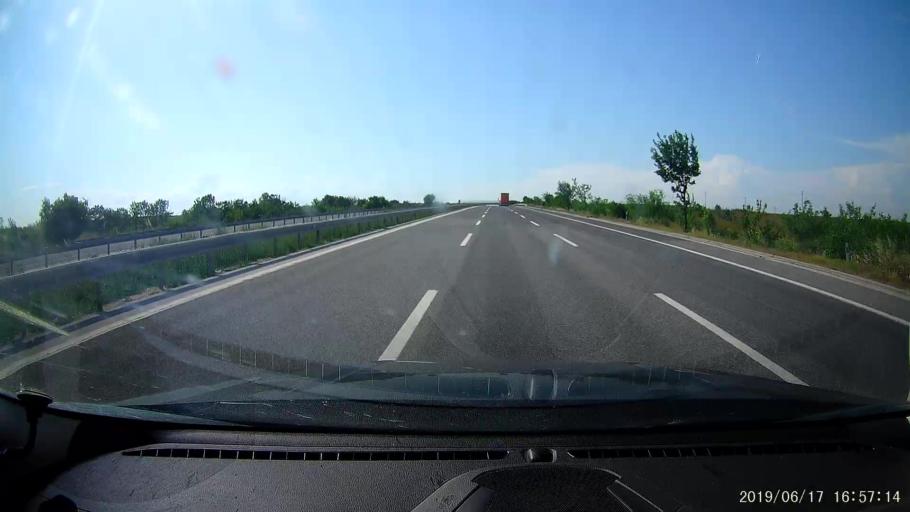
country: TR
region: Edirne
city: Haskoy
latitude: 41.5973
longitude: 26.9188
